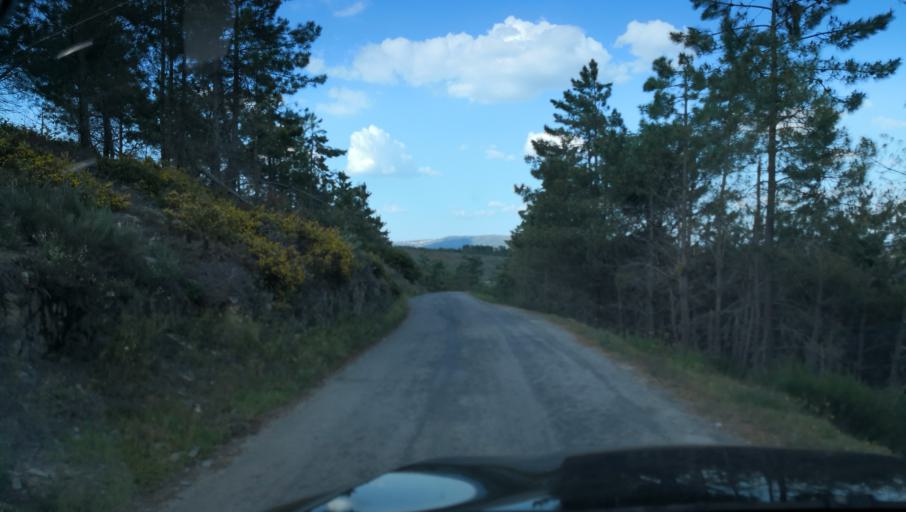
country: PT
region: Vila Real
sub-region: Sabrosa
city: Vilela
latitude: 41.2335
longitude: -7.6692
